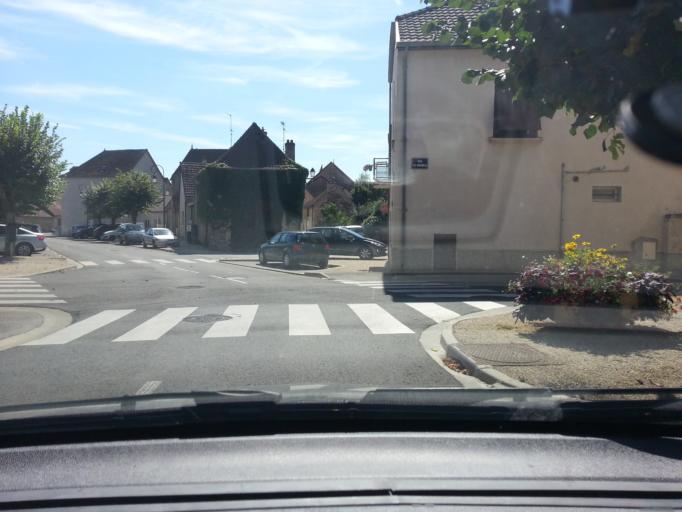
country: FR
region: Bourgogne
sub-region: Departement de Saone-et-Loire
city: Givry
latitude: 46.7829
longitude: 4.7414
